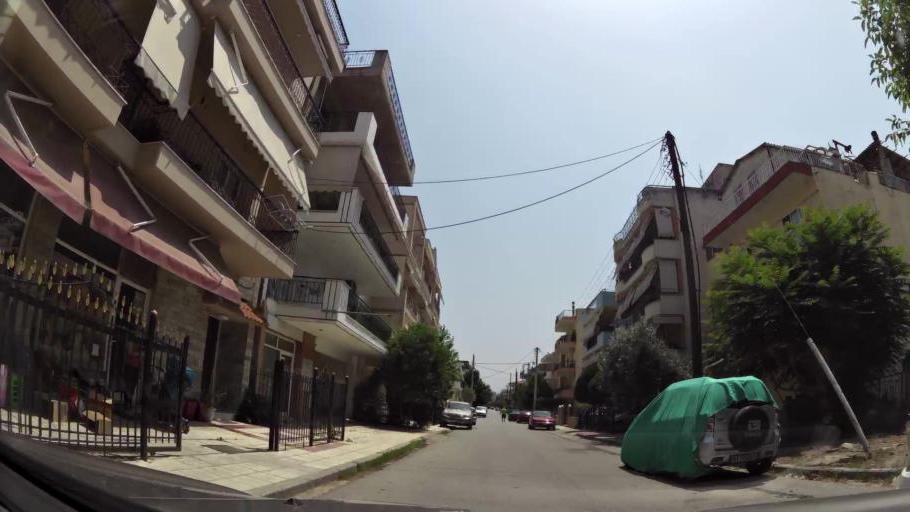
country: GR
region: Central Macedonia
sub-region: Nomos Thessalonikis
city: Evosmos
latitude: 40.6696
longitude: 22.9020
